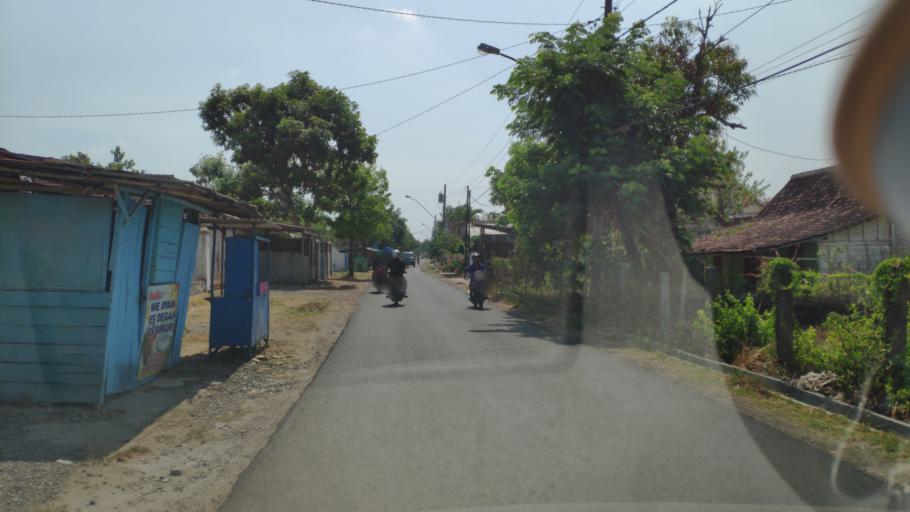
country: ID
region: Central Java
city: Mlangsen
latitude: -6.9788
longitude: 111.4151
